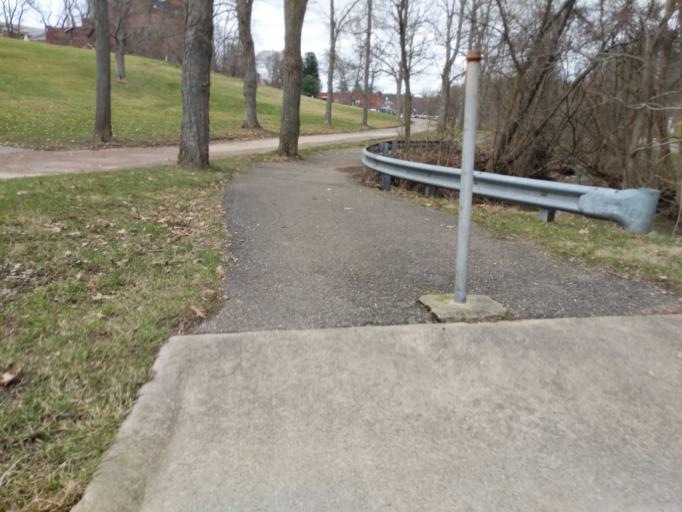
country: US
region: Ohio
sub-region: Athens County
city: Athens
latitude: 39.3182
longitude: -82.1116
